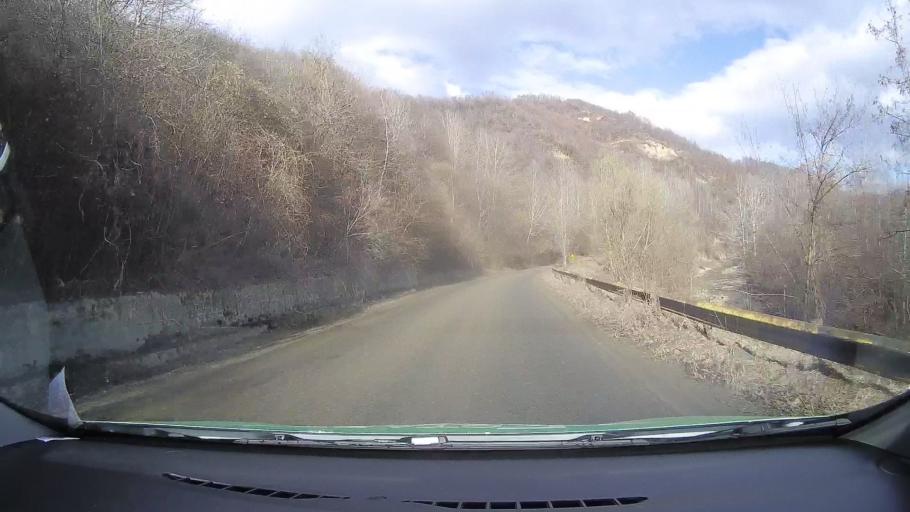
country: RO
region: Dambovita
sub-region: Oras Pucioasa
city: Pucioasa
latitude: 45.1009
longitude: 25.4412
